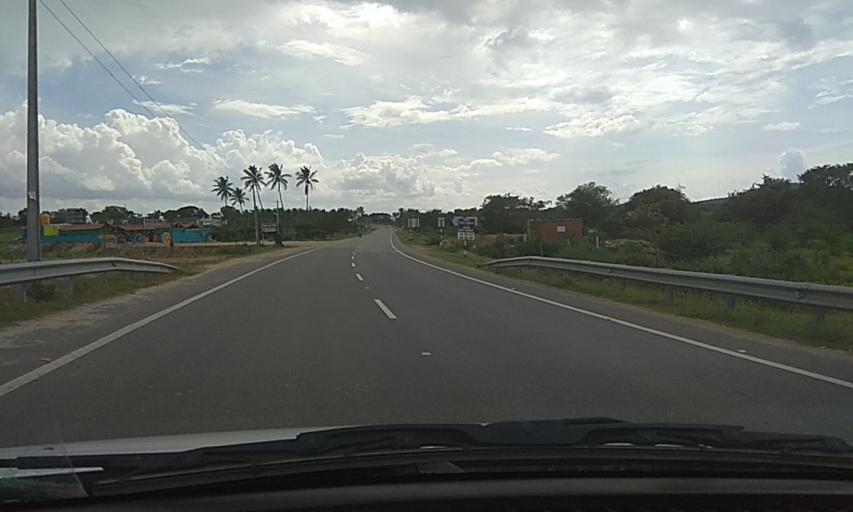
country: IN
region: Karnataka
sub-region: Tumkur
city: Kunigal
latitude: 12.8386
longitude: 77.0337
